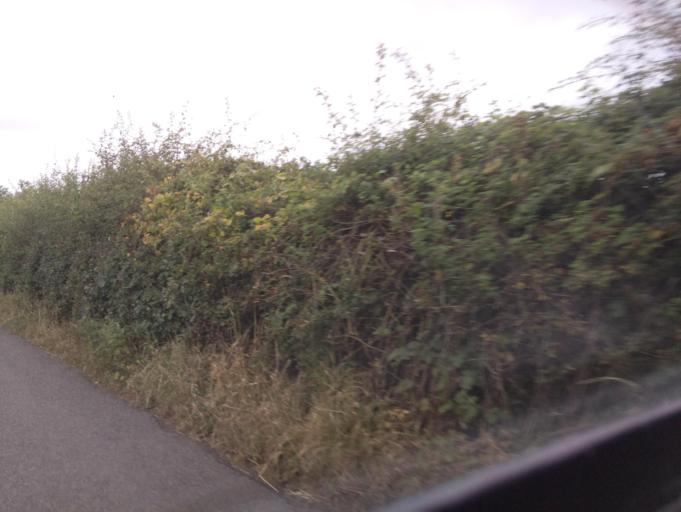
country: GB
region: England
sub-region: Leicestershire
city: Ashby de la Zouch
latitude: 52.7750
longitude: -1.5062
